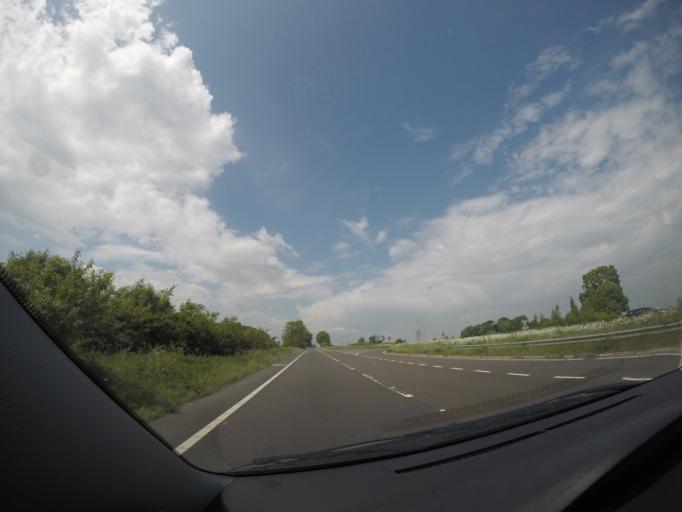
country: GB
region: England
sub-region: North Yorkshire
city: Catterick Garrison
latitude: 54.4617
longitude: -1.7293
